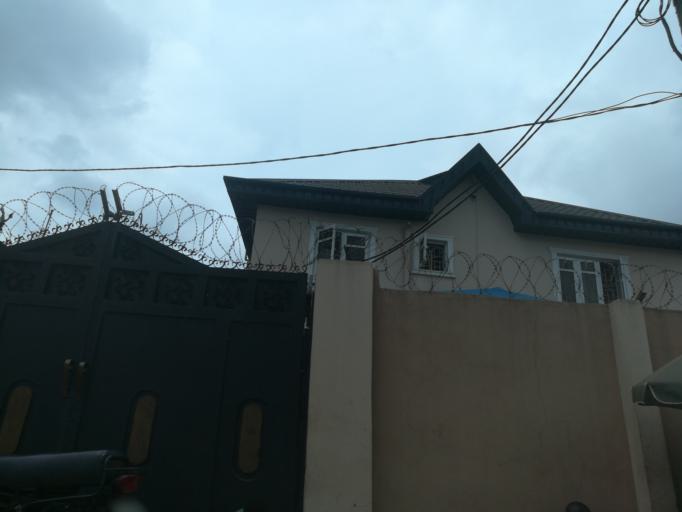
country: NG
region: Lagos
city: Oshodi
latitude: 6.5547
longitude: 3.3320
